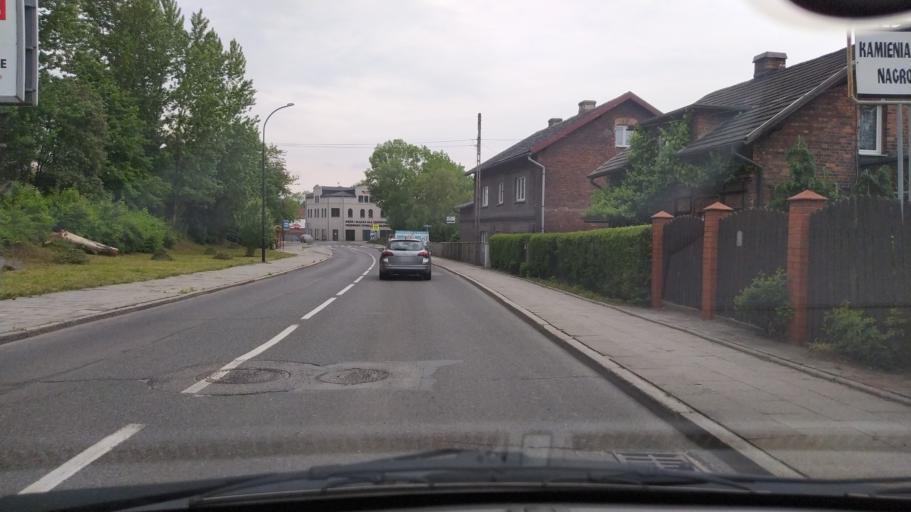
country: PL
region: Silesian Voivodeship
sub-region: Powiat gliwicki
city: Przyszowice
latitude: 50.2893
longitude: 18.7277
